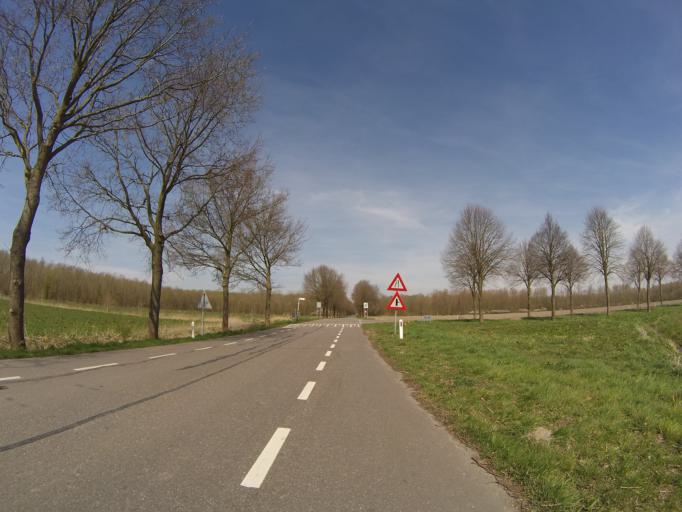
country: NL
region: Flevoland
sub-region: Gemeente Zeewolde
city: Zeewolde
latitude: 52.3243
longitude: 5.4999
